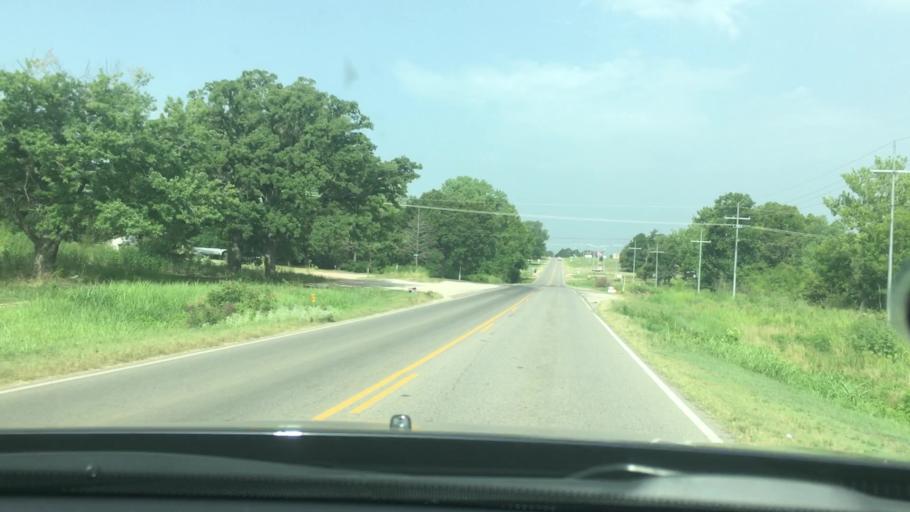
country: US
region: Oklahoma
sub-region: Pontotoc County
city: Ada
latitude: 34.7821
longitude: -96.7735
